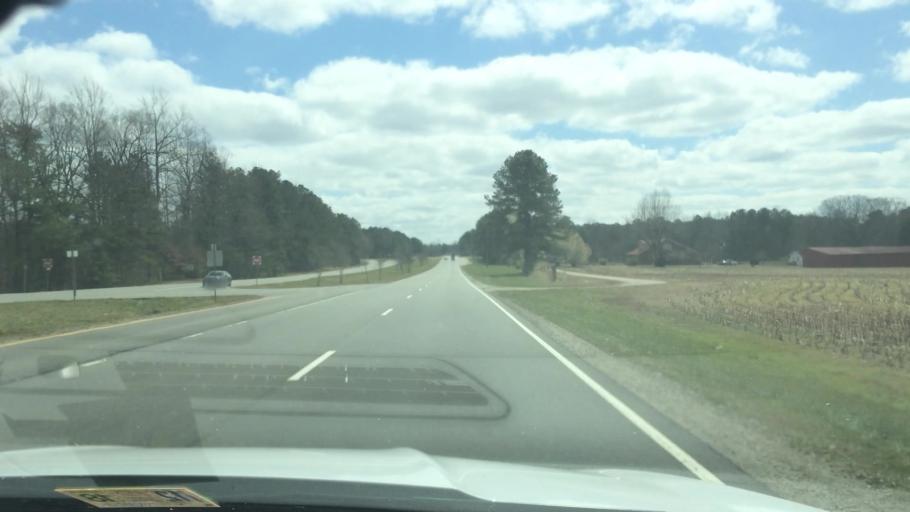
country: US
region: Virginia
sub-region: King William County
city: West Point
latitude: 37.4268
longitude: -76.8286
